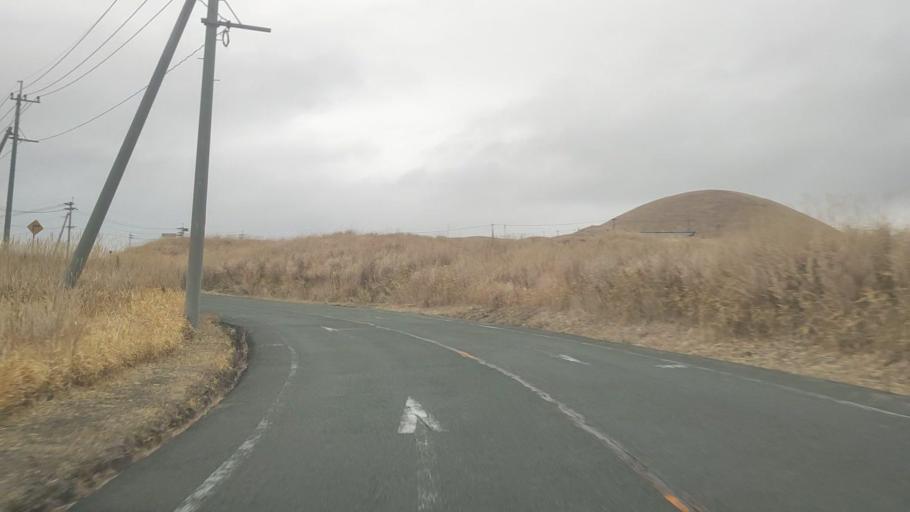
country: JP
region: Kumamoto
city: Aso
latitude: 32.9025
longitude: 131.0349
